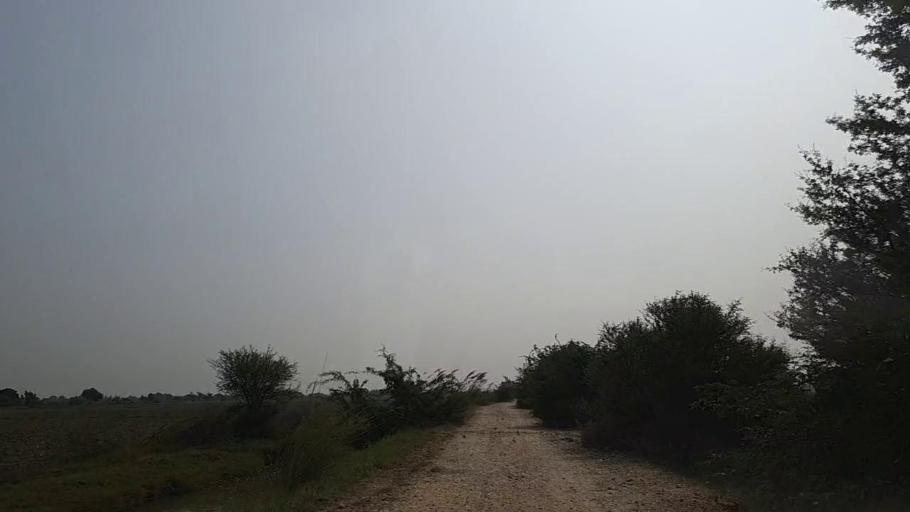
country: PK
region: Sindh
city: Mirpur Sakro
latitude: 24.5990
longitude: 67.7157
